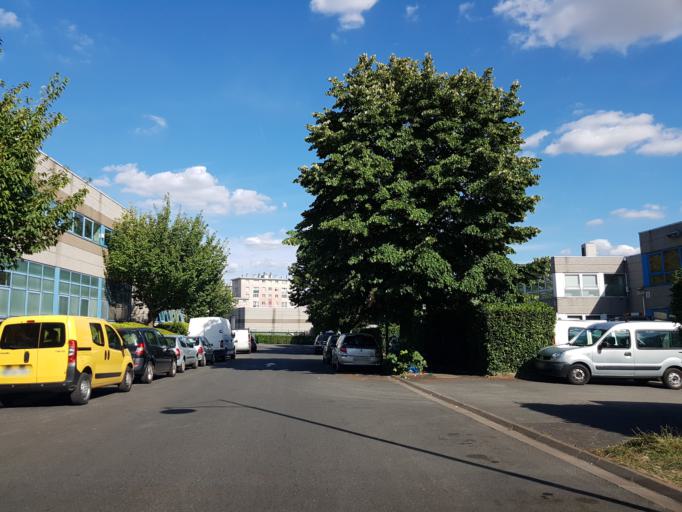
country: FR
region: Ile-de-France
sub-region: Departement du Val-de-Marne
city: Villejuif
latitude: 48.7876
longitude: 2.3503
